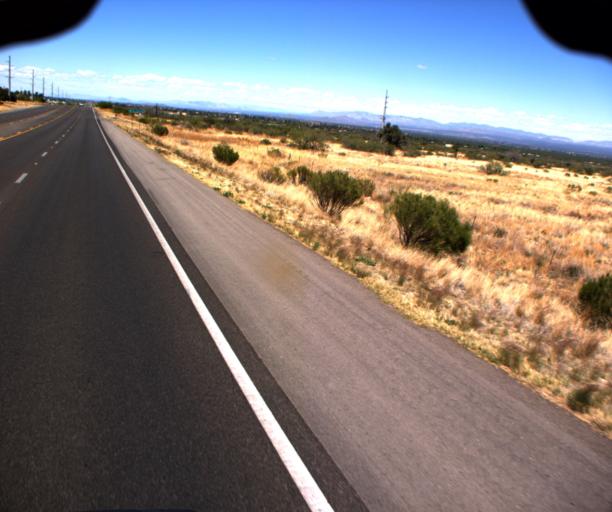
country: US
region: Arizona
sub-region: Cochise County
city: Sierra Vista Southeast
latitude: 31.4510
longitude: -110.2573
